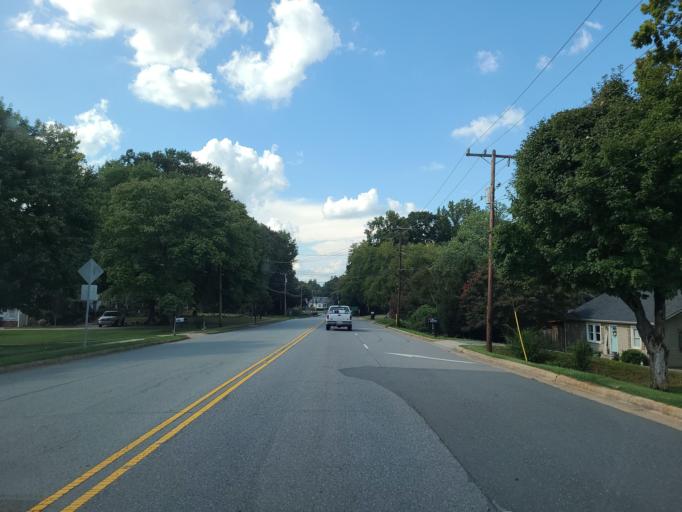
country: US
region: North Carolina
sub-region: Gaston County
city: Lowell
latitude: 35.2726
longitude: -81.0967
